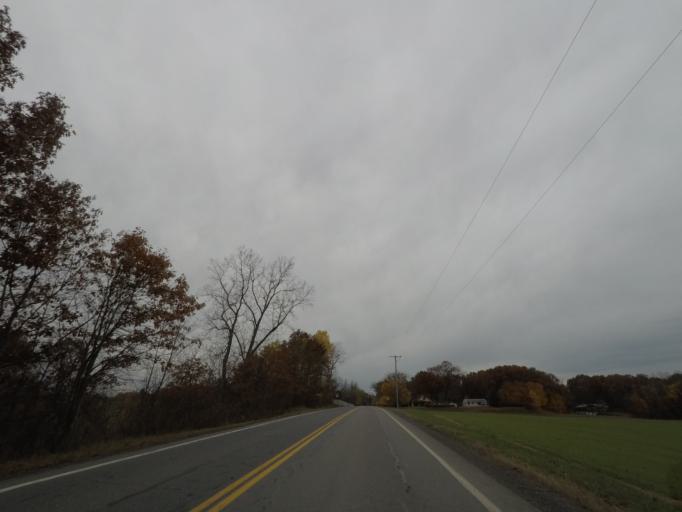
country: US
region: New York
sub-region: Saratoga County
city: Mechanicville
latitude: 42.8528
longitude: -73.7152
